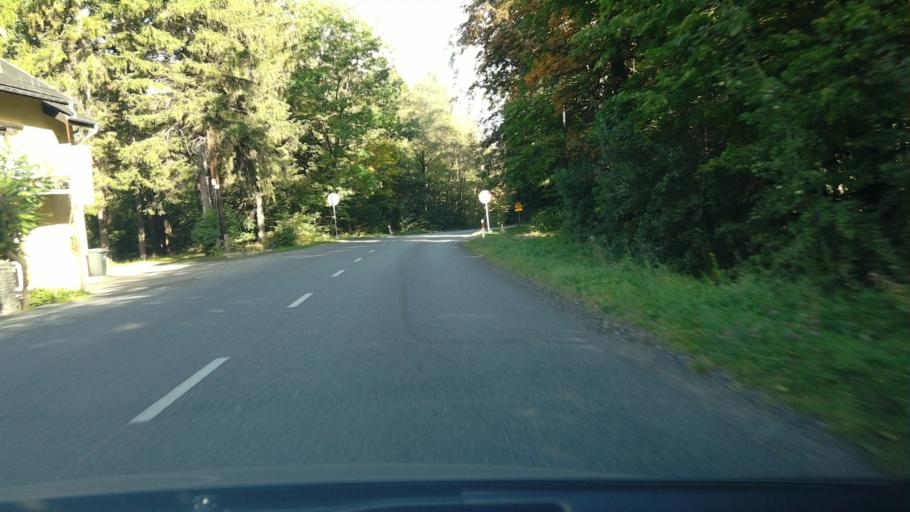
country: PL
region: Lower Silesian Voivodeship
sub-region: Powiat jeleniogorski
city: Karpacz
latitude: 50.7950
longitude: 15.7628
